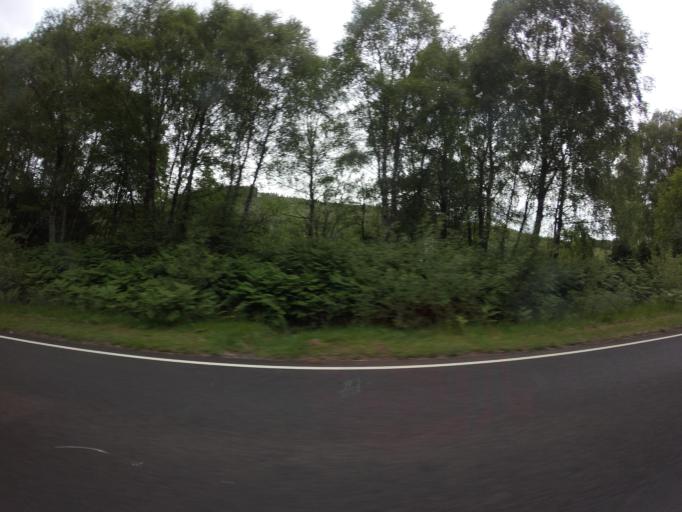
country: GB
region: Scotland
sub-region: Highland
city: Dingwall
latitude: 57.6636
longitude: -4.6716
